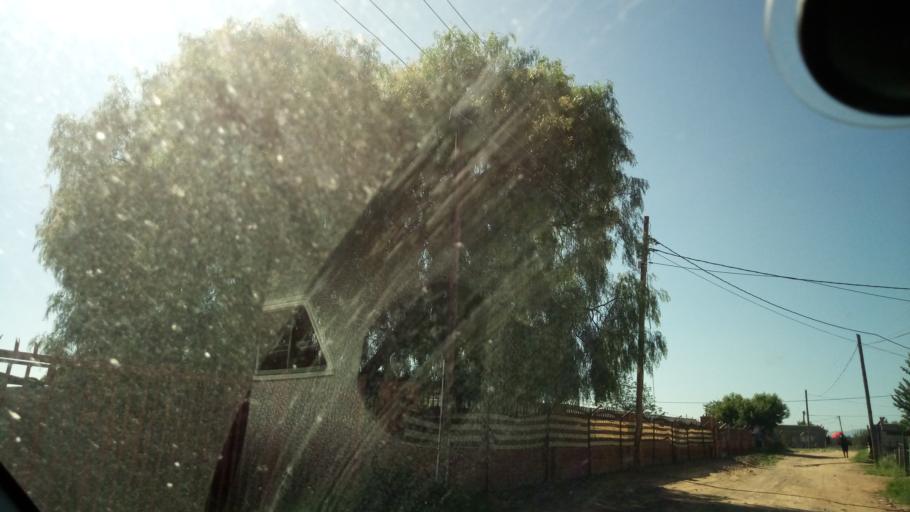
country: LS
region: Maseru
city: Maseru
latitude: -29.3508
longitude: 27.5360
